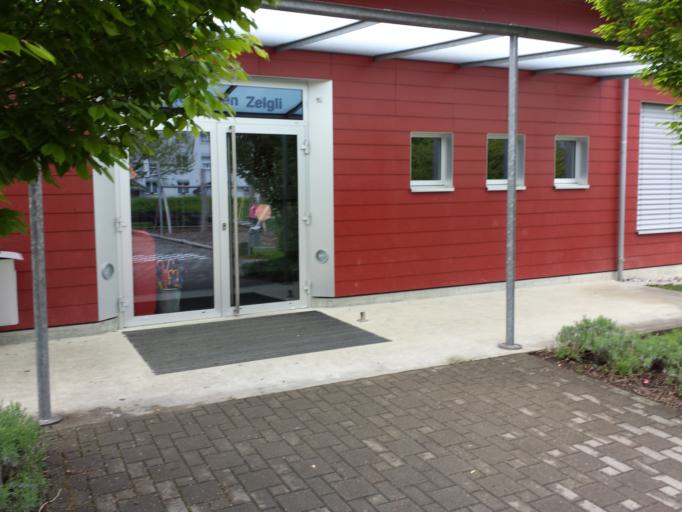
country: CH
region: Thurgau
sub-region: Arbon District
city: Romanshorn
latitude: 47.5673
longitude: 9.3727
